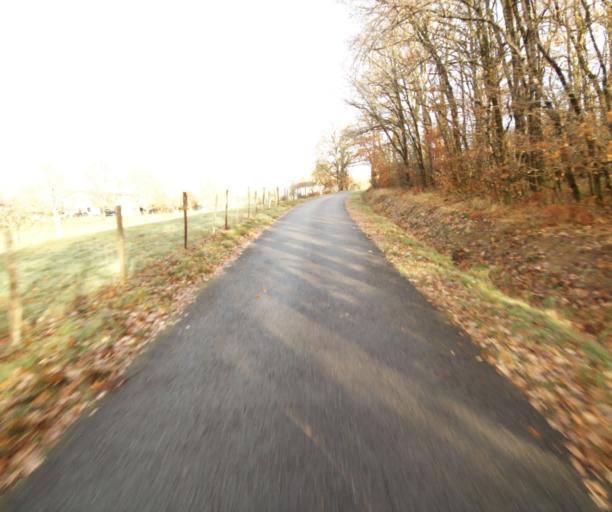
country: FR
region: Limousin
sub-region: Departement de la Correze
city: Saint-Mexant
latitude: 45.2637
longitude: 1.6293
